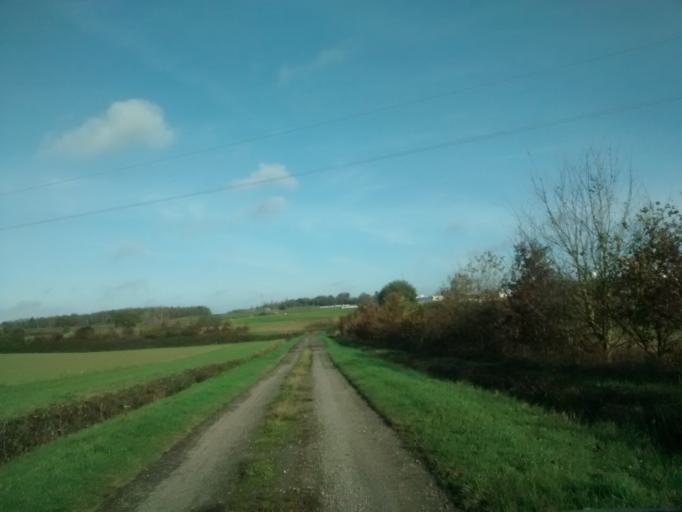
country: FR
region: Brittany
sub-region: Departement d'Ille-et-Vilaine
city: Cesson-Sevigne
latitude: 48.1041
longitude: -1.5911
